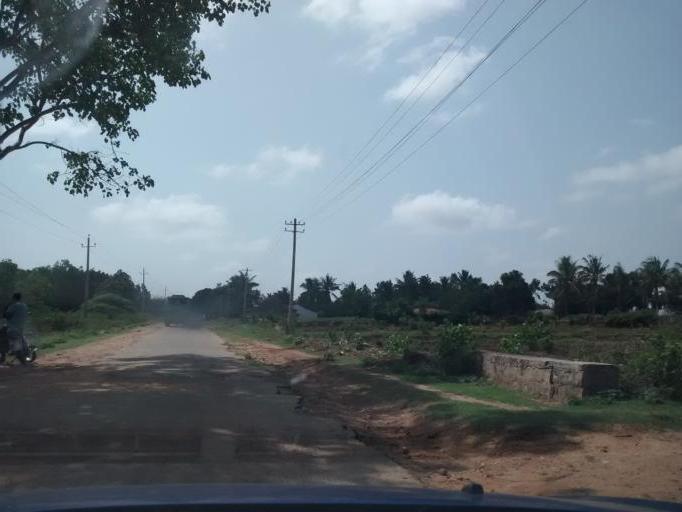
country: IN
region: Karnataka
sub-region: Hassan
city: Hole Narsipur
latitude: 12.6955
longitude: 76.1781
